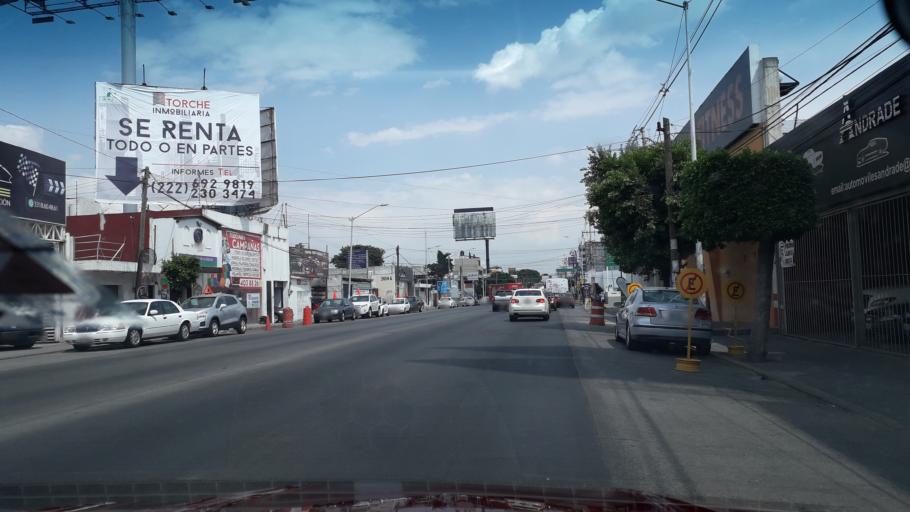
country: MX
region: Puebla
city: Puebla
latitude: 19.0447
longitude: -98.2292
